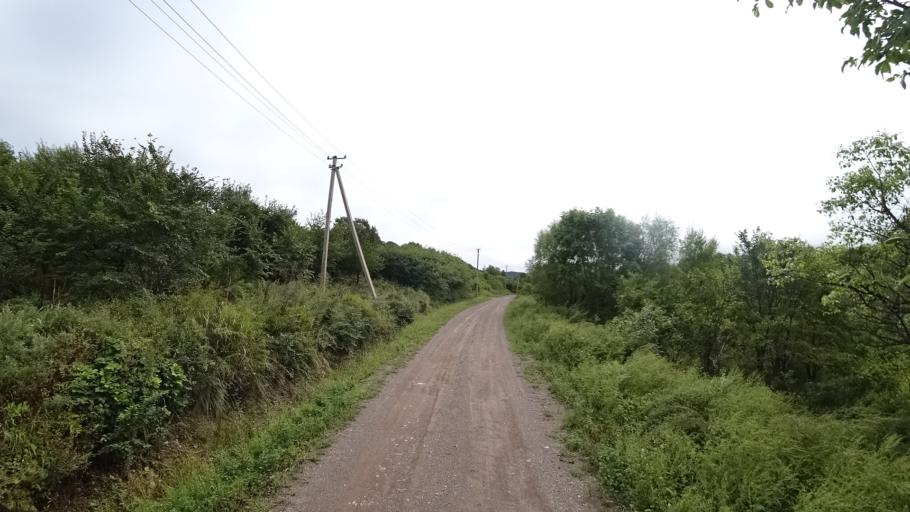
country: RU
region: Primorskiy
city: Monastyrishche
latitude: 44.1675
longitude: 132.5400
